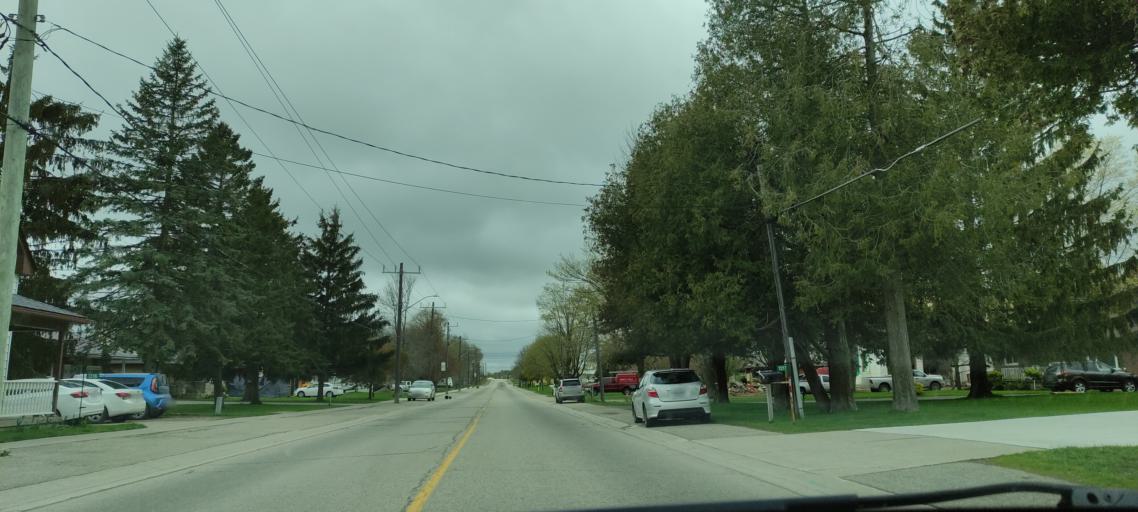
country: CA
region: Ontario
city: Stratford
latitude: 43.4783
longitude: -80.7720
